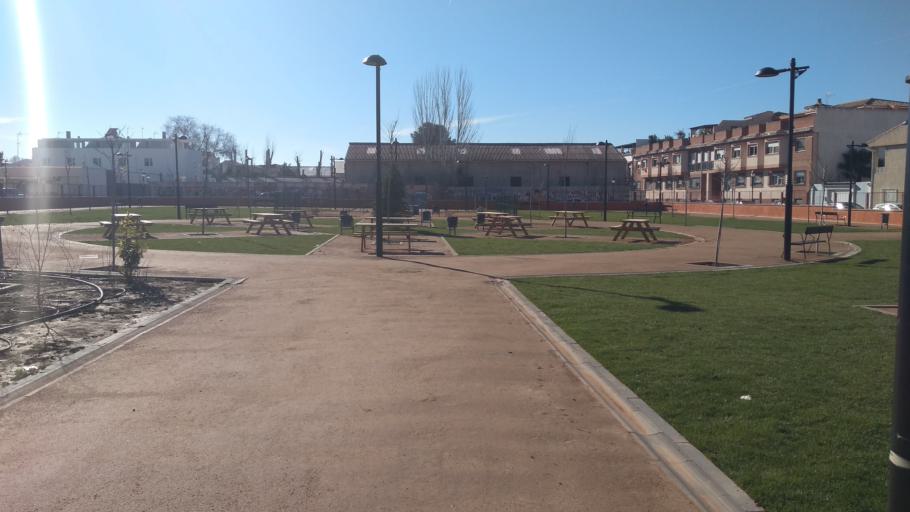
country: ES
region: Andalusia
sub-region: Provincia de Granada
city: Armilla
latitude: 37.1429
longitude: -3.6171
